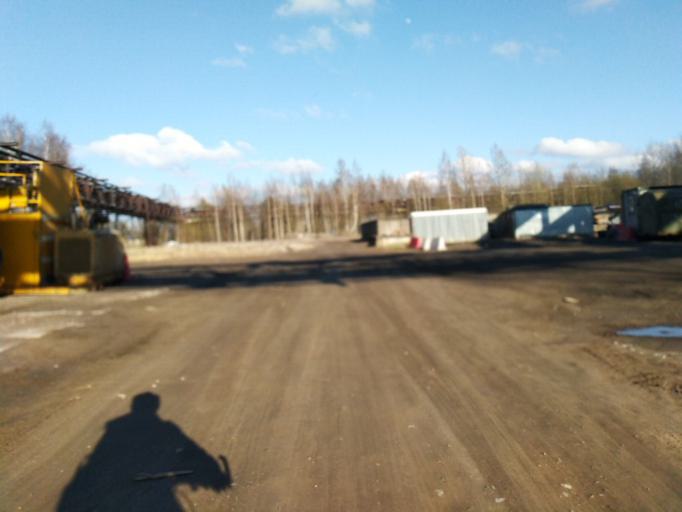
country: RU
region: Leningrad
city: Novoye Devyatkino
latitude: 60.0719
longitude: 30.4792
